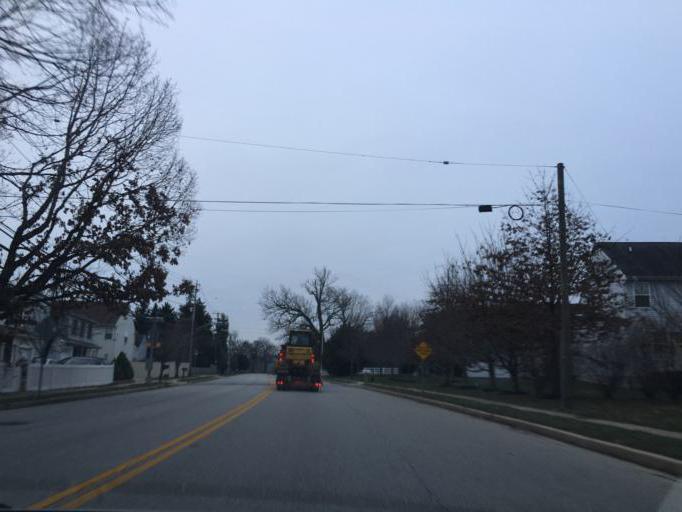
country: US
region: Maryland
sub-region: Baltimore County
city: Catonsville
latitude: 39.2942
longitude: -76.7532
